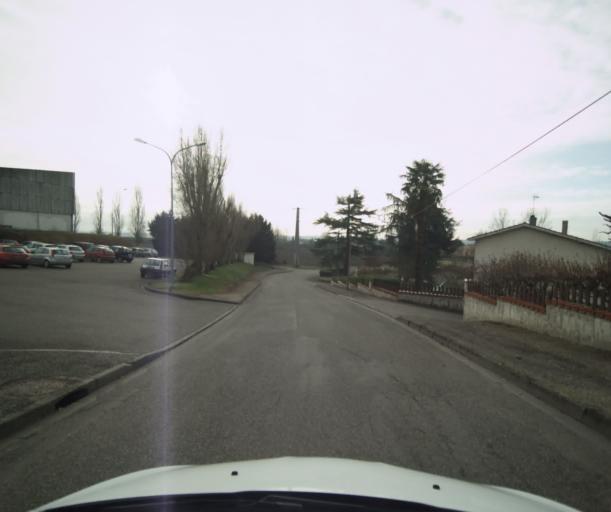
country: FR
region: Midi-Pyrenees
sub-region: Departement du Tarn-et-Garonne
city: Castelsarrasin
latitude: 44.0316
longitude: 1.1176
